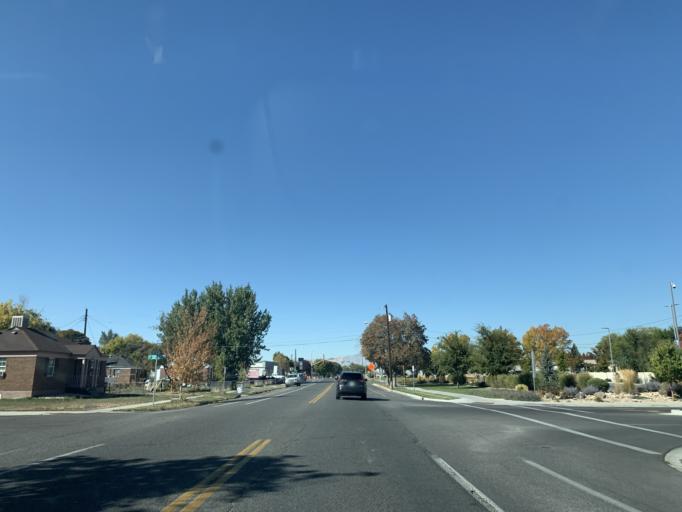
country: US
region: Utah
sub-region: Utah County
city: Provo
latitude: 40.2443
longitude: -111.6649
